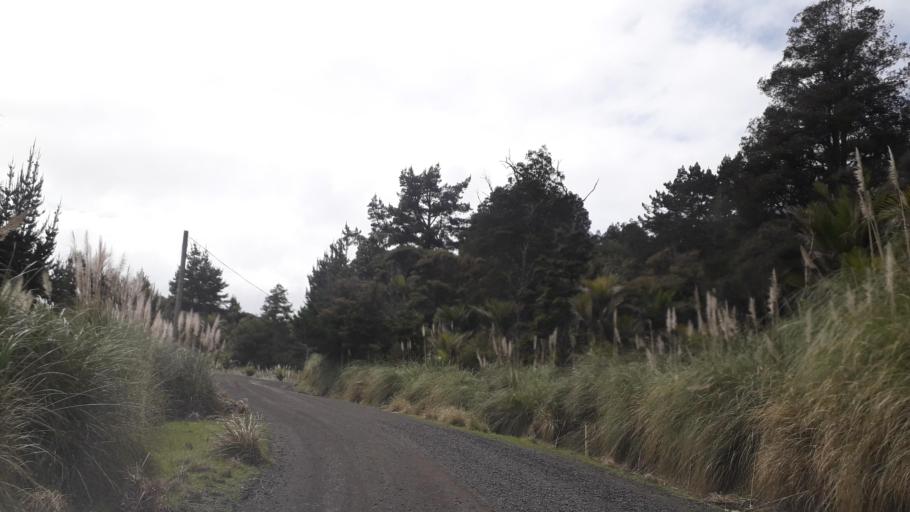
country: NZ
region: Northland
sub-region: Far North District
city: Kaitaia
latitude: -35.3700
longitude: 173.4118
